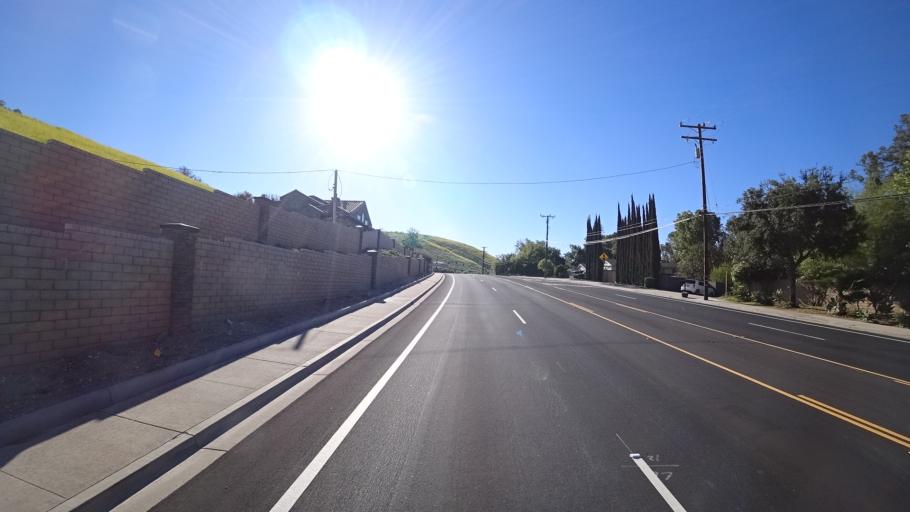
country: US
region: California
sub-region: Ventura County
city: Thousand Oaks
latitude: 34.1801
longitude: -118.8429
